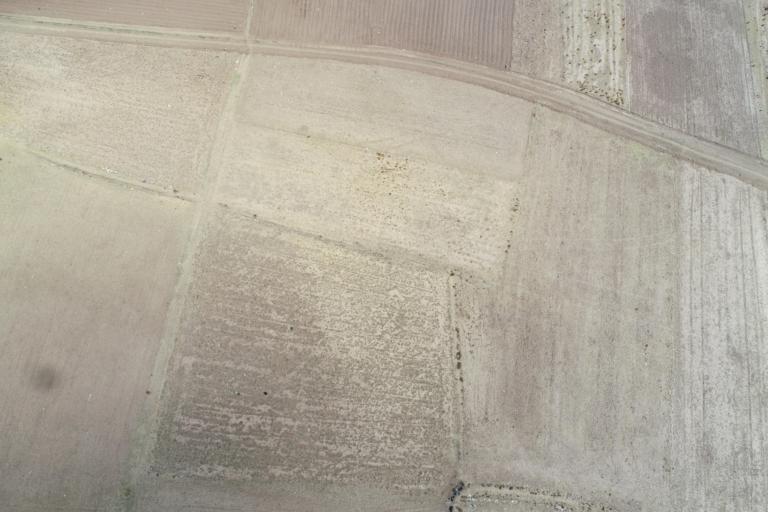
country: BO
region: La Paz
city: Achacachi
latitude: -15.9136
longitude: -68.8843
